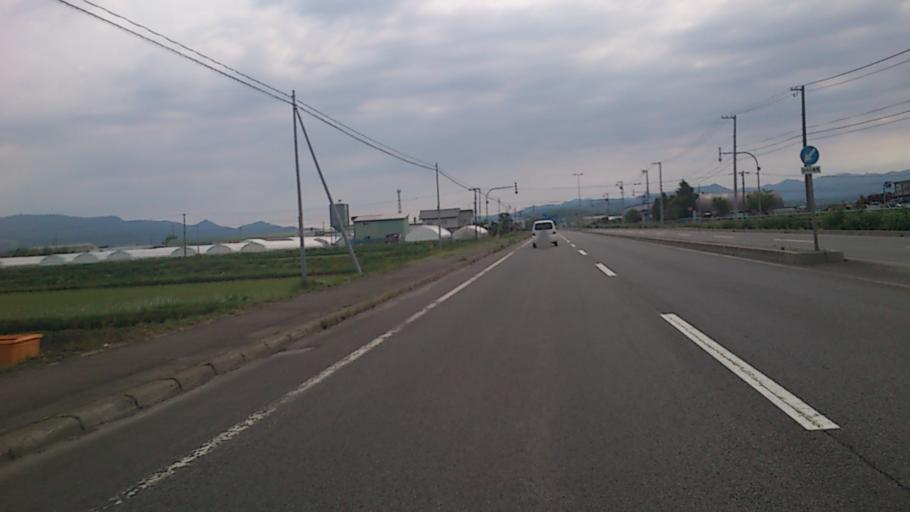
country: JP
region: Hokkaido
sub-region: Asahikawa-shi
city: Asahikawa
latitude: 43.8507
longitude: 142.4981
